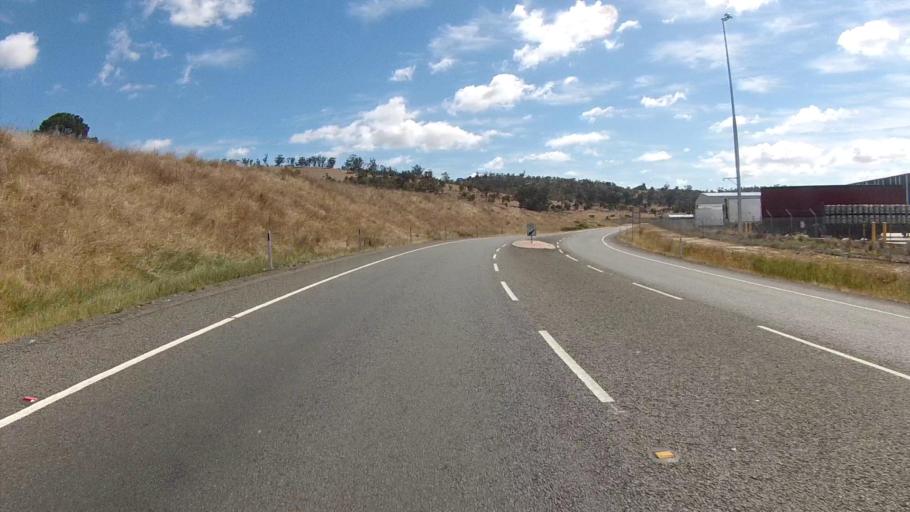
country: AU
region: Tasmania
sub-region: Brighton
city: Bridgewater
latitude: -42.7177
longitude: 147.2256
